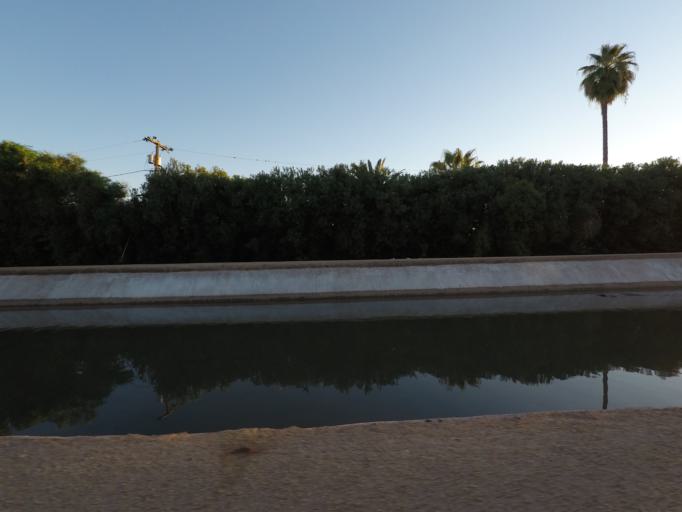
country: US
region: Arizona
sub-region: Maricopa County
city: Phoenix
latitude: 33.5008
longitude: -112.0940
